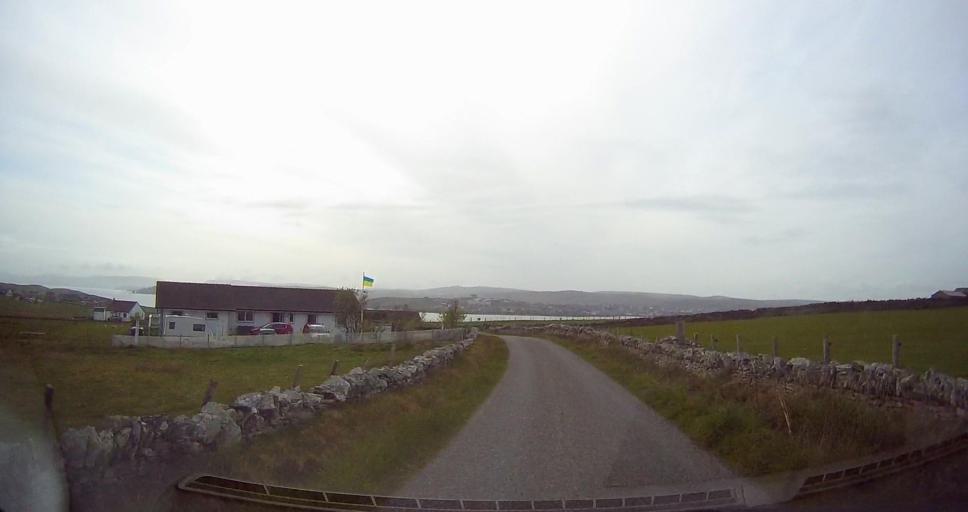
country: GB
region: Scotland
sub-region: Shetland Islands
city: Shetland
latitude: 60.1512
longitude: -1.1007
